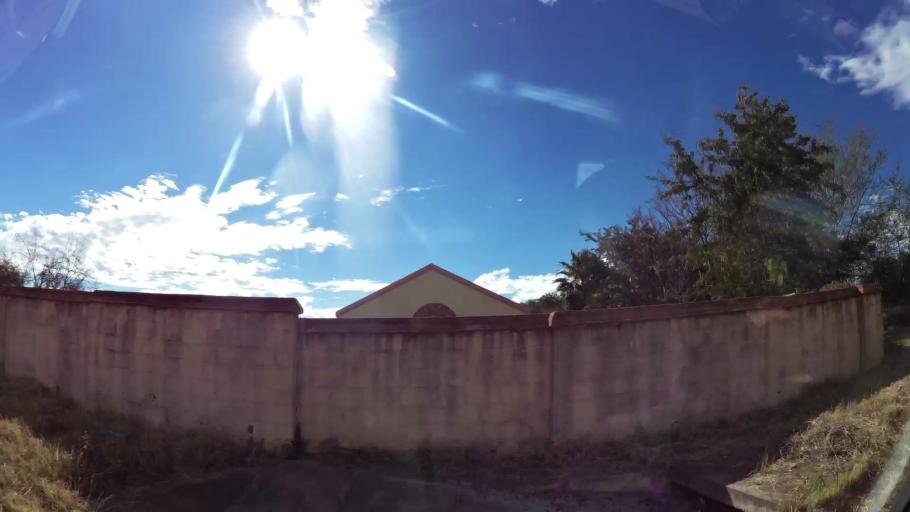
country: ZA
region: Limpopo
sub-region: Waterberg District Municipality
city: Bela-Bela
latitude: -24.8765
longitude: 28.2934
